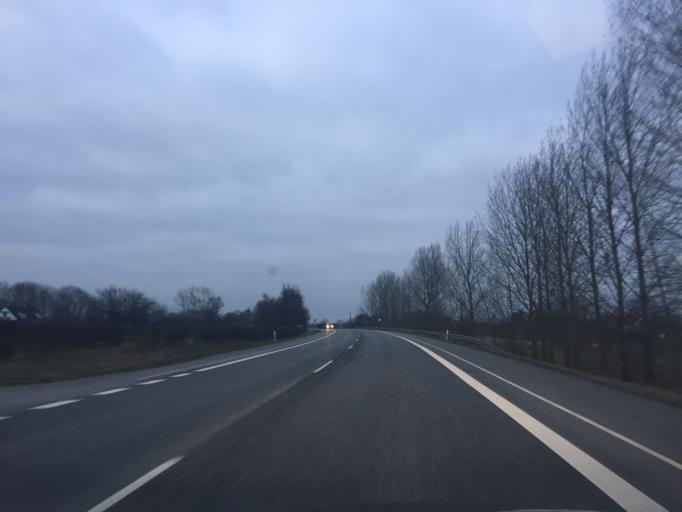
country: DK
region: Capital Region
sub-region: Halsnaes Kommune
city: Frederiksvaerk
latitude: 55.9107
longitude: 12.0597
